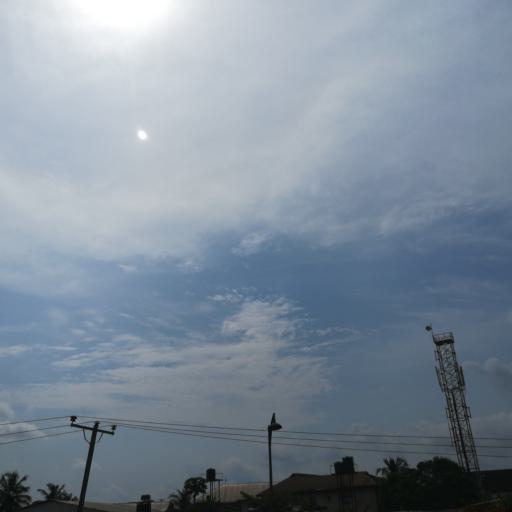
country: NG
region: Rivers
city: Port Harcourt
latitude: 4.8583
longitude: 7.0221
